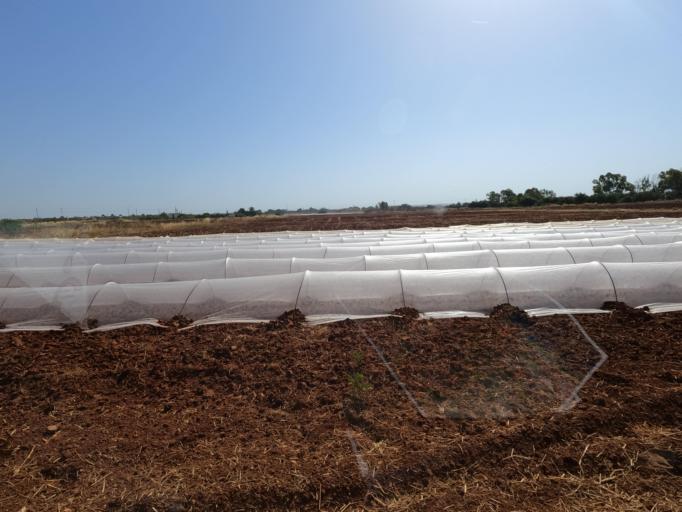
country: CY
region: Ammochostos
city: Liopetri
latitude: 34.9870
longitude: 33.8815
